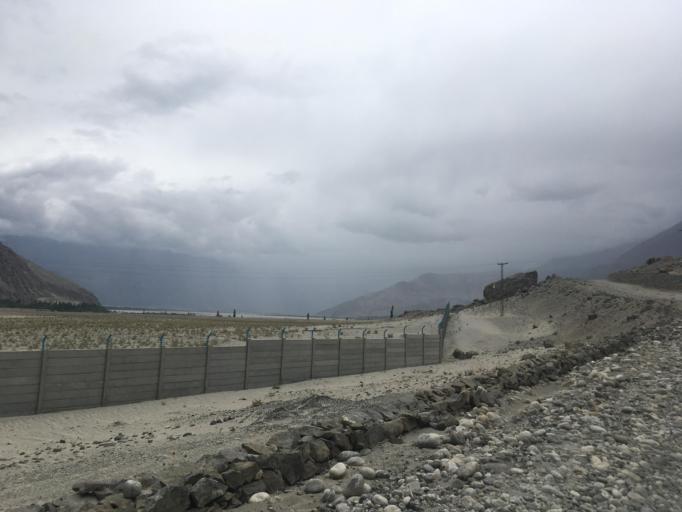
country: PK
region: Gilgit-Baltistan
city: Skardu
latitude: 35.3177
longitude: 75.6571
